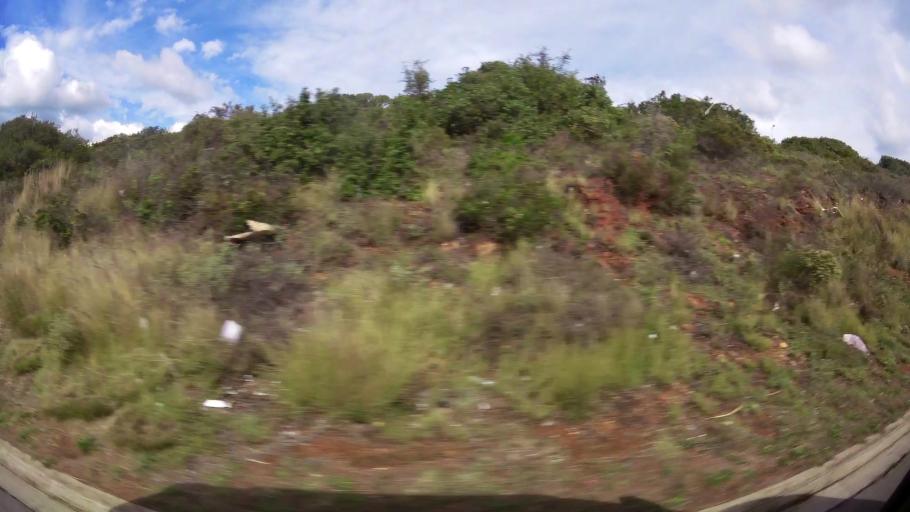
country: ZA
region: Eastern Cape
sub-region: Nelson Mandela Bay Metropolitan Municipality
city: Port Elizabeth
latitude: -33.9387
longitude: 25.5752
